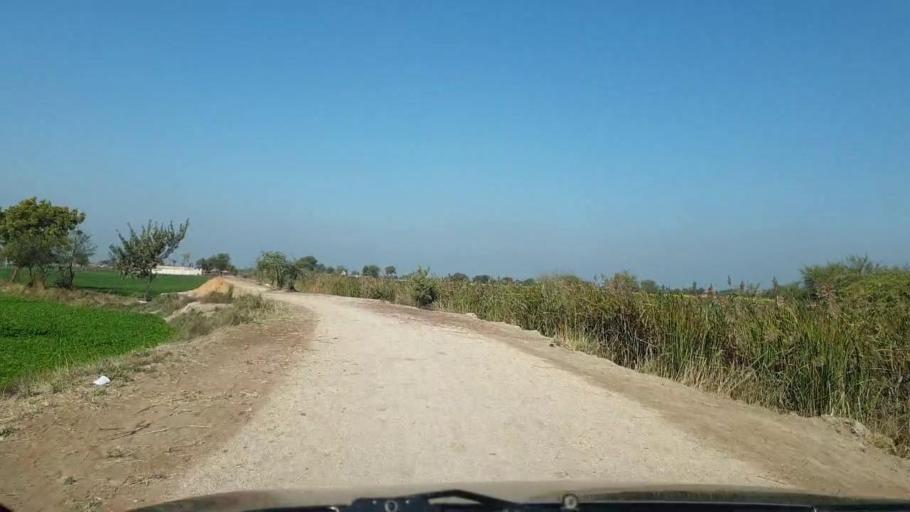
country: PK
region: Sindh
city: Sinjhoro
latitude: 25.9709
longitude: 68.7529
